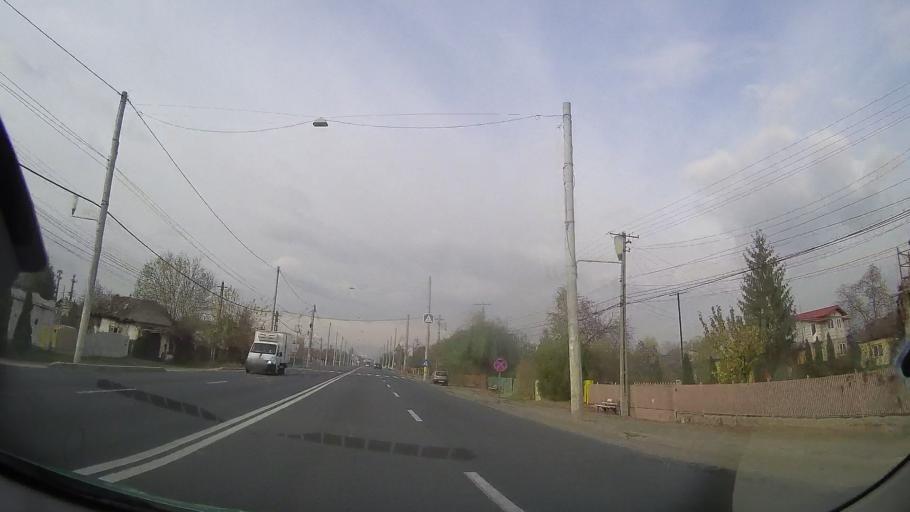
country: RO
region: Prahova
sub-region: Comuna Barcanesti
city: Tatarani
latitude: 44.8957
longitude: 26.0429
